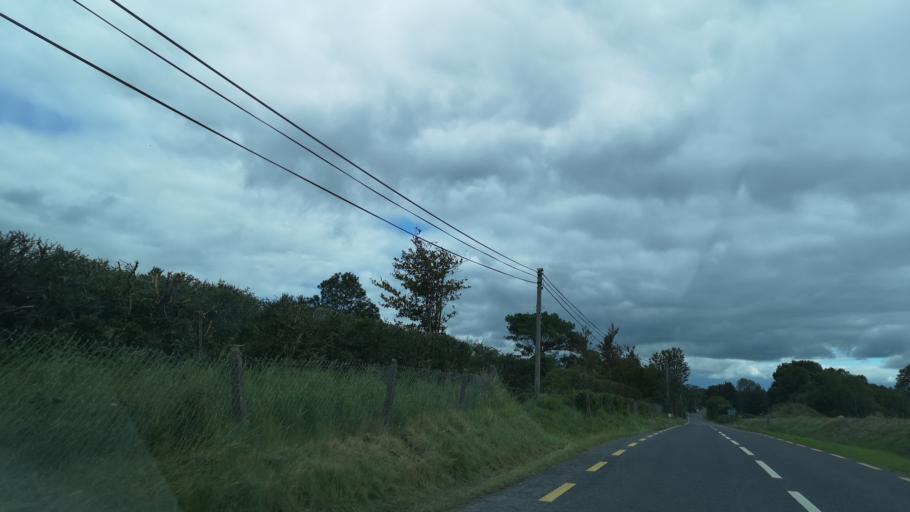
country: IE
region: Connaught
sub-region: County Galway
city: Ballinasloe
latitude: 53.3038
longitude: -8.1371
